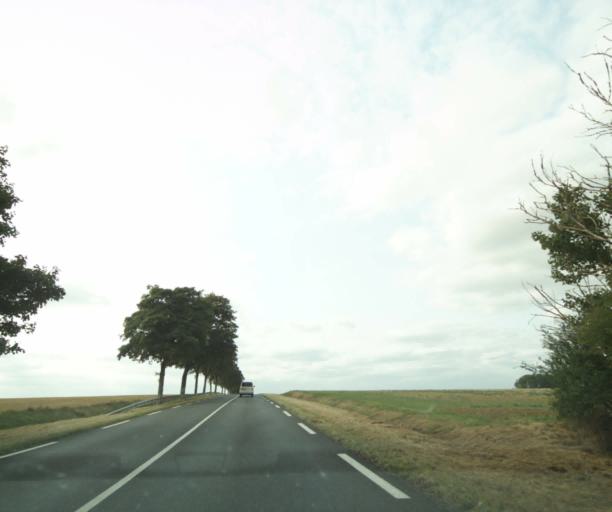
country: FR
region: Centre
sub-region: Departement d'Indre-et-Loire
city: Reignac-sur-Indre
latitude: 47.2313
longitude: 0.8746
